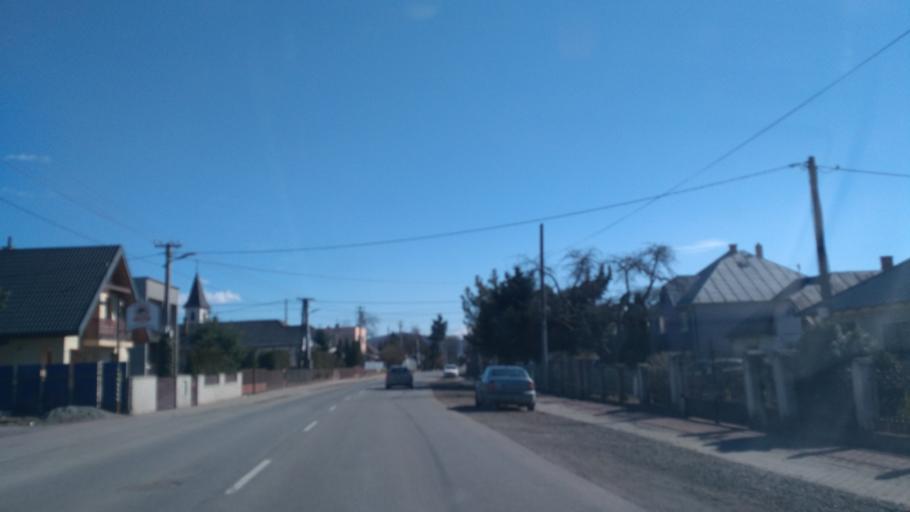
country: SK
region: Kosicky
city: Kosice
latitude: 48.6376
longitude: 21.2956
